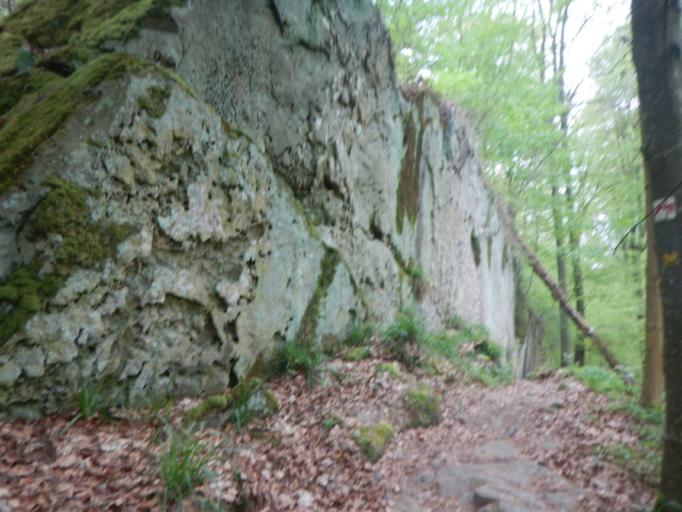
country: LU
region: Grevenmacher
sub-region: Canton d'Echternach
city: Berdorf
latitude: 49.8057
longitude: 6.3250
